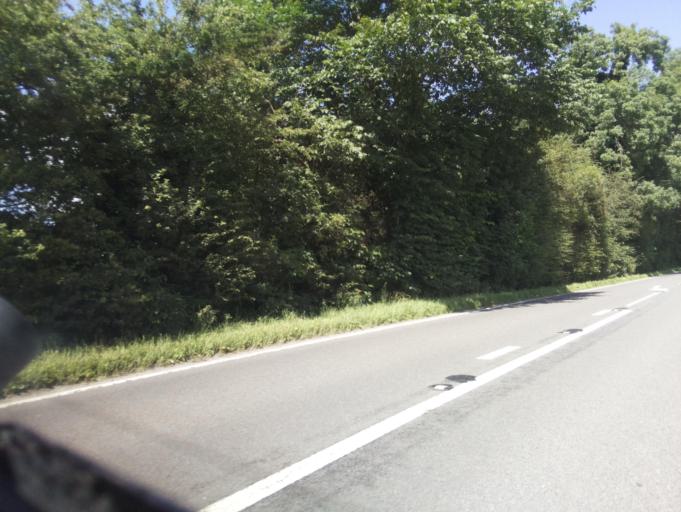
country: GB
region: England
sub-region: Derbyshire
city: Ashbourne
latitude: 53.0333
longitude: -1.7364
